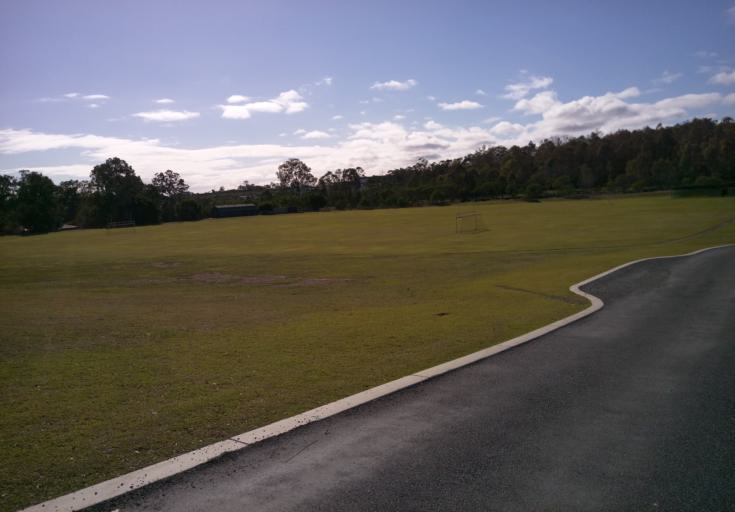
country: AU
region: Queensland
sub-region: Logan
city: Waterford West
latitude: -27.7065
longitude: 153.1489
